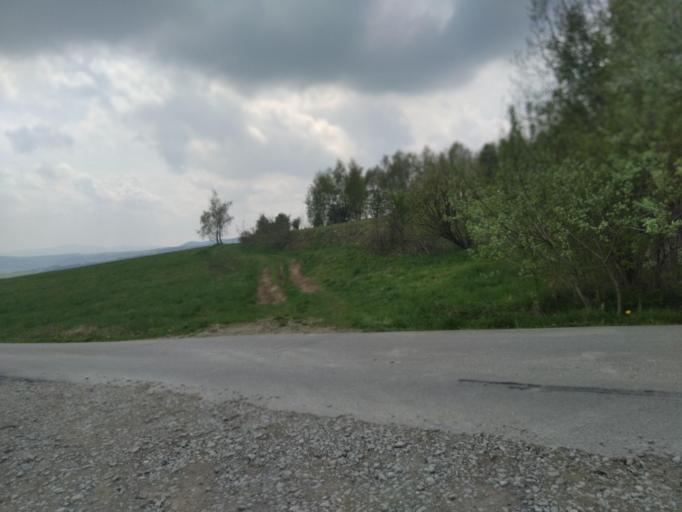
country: PL
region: Subcarpathian Voivodeship
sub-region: Powiat krosnienski
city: Iwonicz-Zdroj
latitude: 49.5399
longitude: 21.7990
